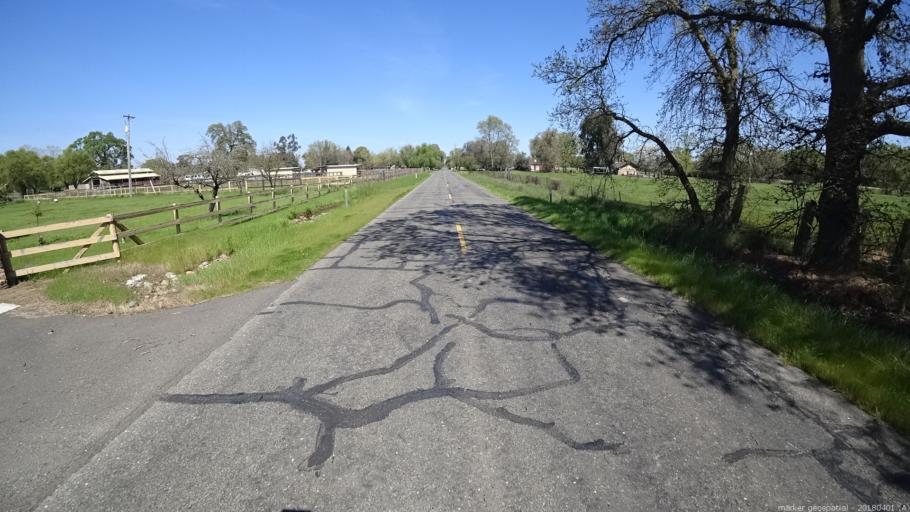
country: US
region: California
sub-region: Sacramento County
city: Wilton
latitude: 38.4365
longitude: -121.1924
